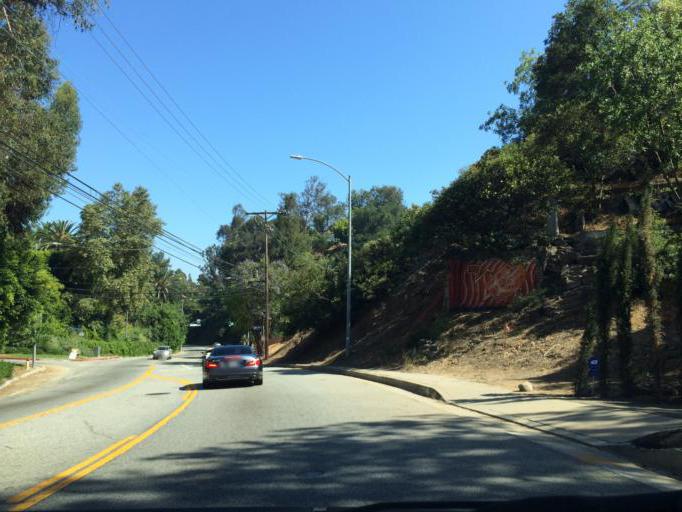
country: US
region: California
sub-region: Los Angeles County
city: West Hollywood
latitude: 34.1161
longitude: -118.3749
